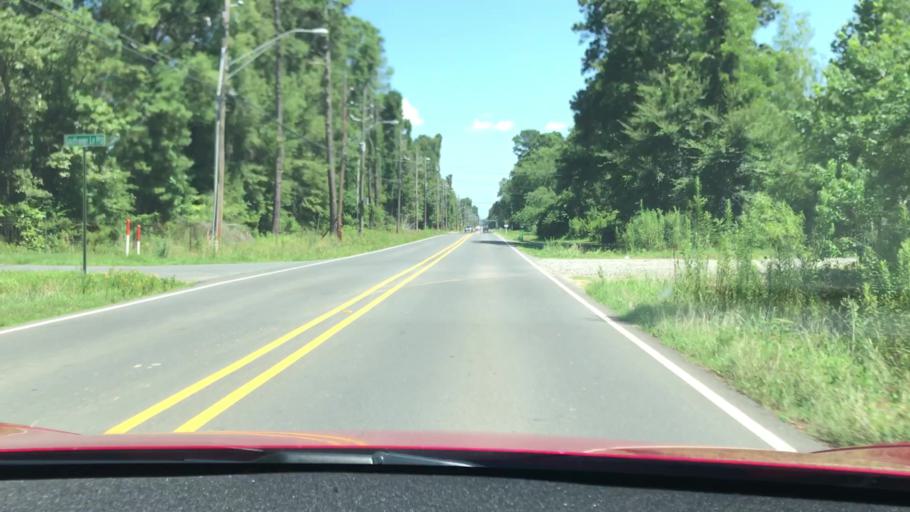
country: US
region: Louisiana
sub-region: De Soto Parish
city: Stonewall
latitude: 32.3500
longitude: -93.7138
